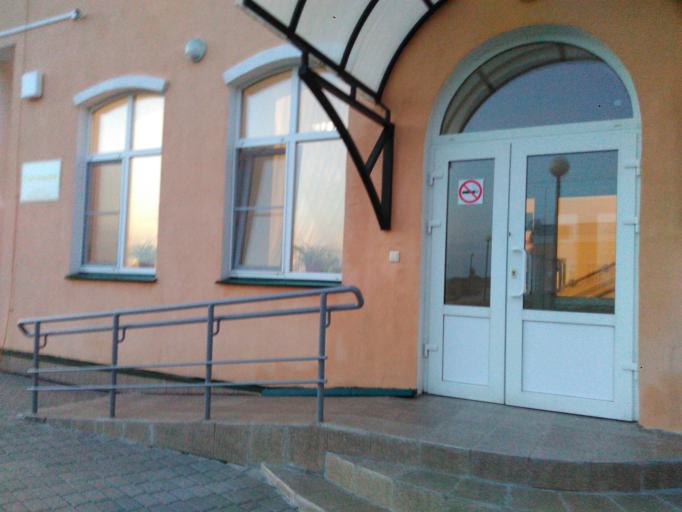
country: RU
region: Penza
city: Lermontovo
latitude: 53.0001
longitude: 43.6726
